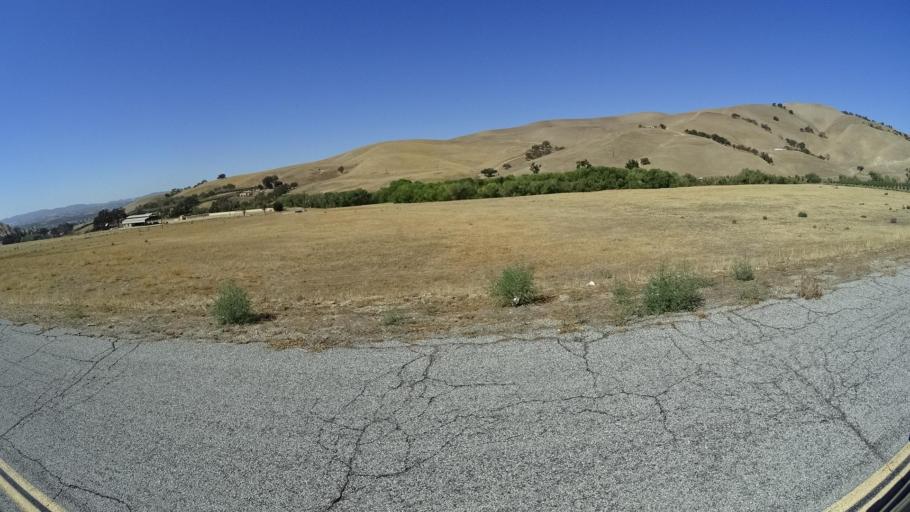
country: US
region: California
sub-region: San Luis Obispo County
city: San Miguel
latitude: 35.7959
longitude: -120.6785
